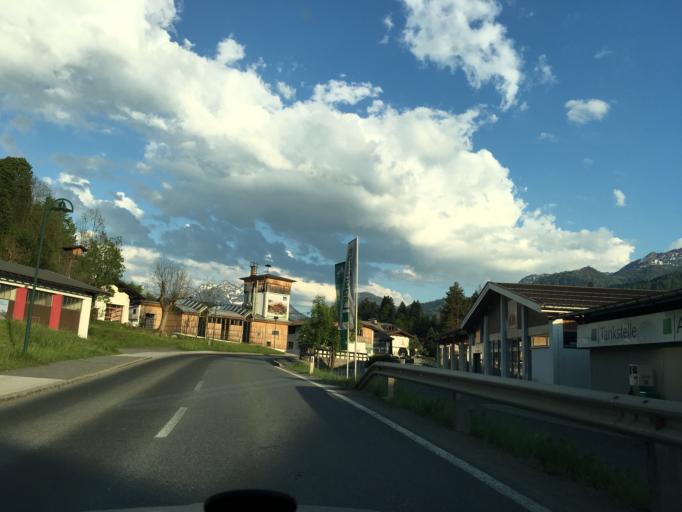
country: AT
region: Tyrol
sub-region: Politischer Bezirk Kitzbuhel
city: Fieberbrunn
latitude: 47.4891
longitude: 12.5282
